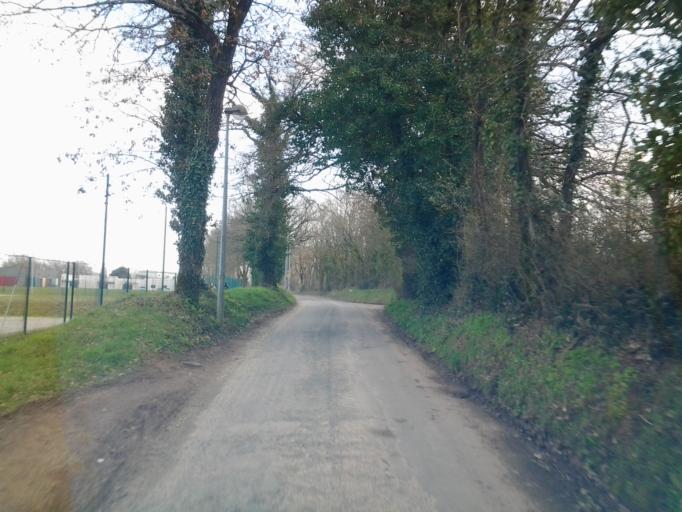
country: FR
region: Pays de la Loire
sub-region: Departement de la Vendee
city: La Roche-sur-Yon
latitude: 46.6593
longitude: -1.4076
